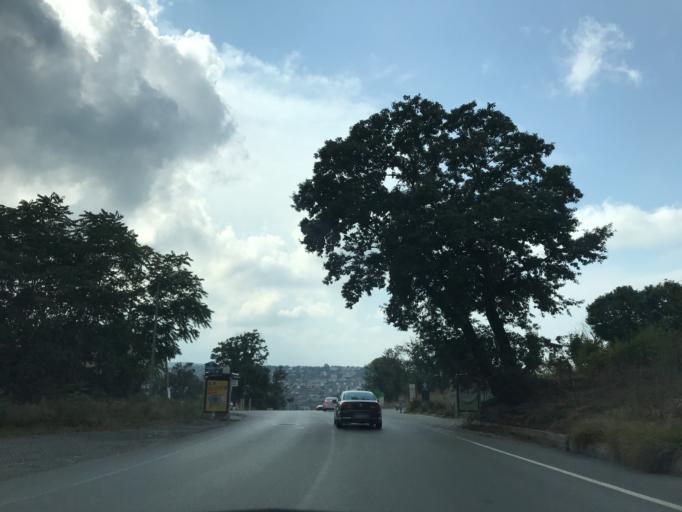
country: TR
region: Istanbul
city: Arikoey
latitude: 41.2105
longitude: 29.0396
